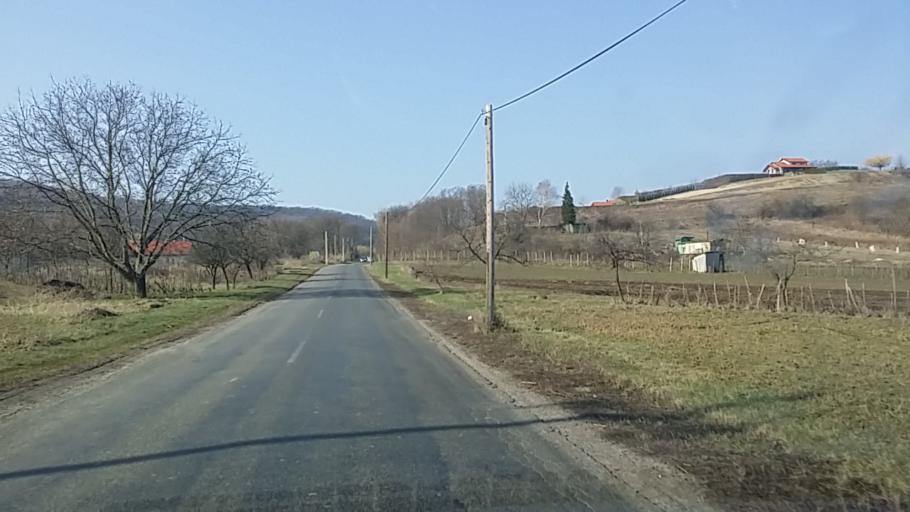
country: HU
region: Komarom-Esztergom
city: Tat
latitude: 47.7332
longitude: 18.6194
